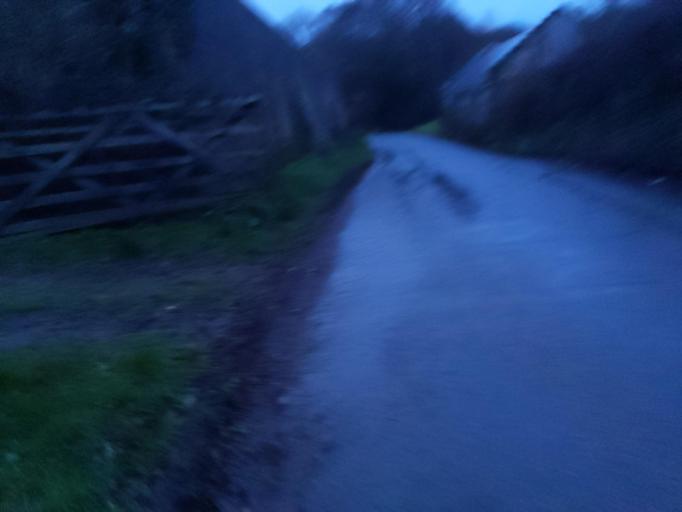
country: GB
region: England
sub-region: Devon
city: Yealmpton
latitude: 50.3398
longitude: -4.0111
